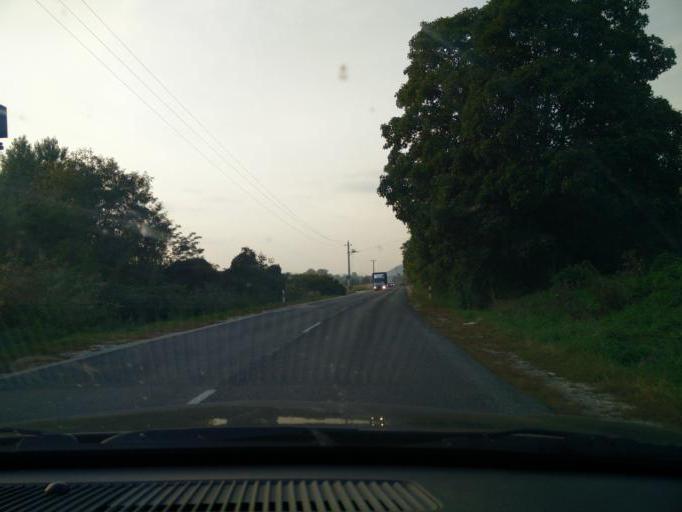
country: HU
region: Pest
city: Piliscsaba
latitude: 47.6371
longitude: 18.8168
